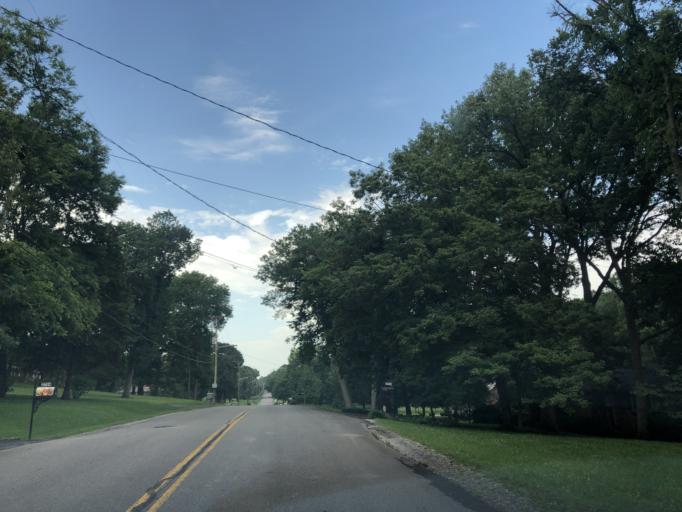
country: US
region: Tennessee
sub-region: Davidson County
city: Lakewood
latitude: 36.1832
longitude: -86.6900
